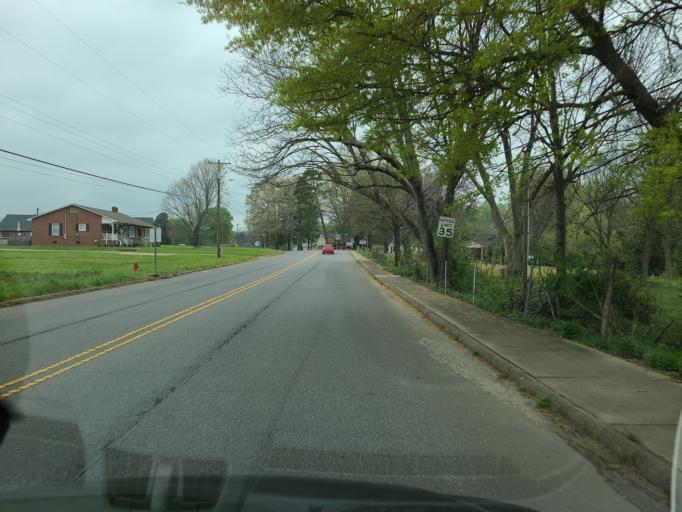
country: US
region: North Carolina
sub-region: Gaston County
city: Cherryville
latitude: 35.4262
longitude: -81.4952
